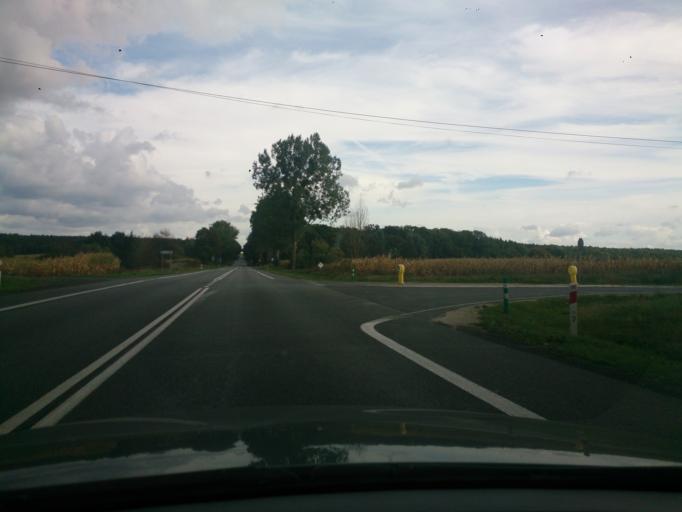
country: PL
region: Kujawsko-Pomorskie
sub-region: Powiat swiecki
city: Jezewo
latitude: 53.4393
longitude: 18.5479
